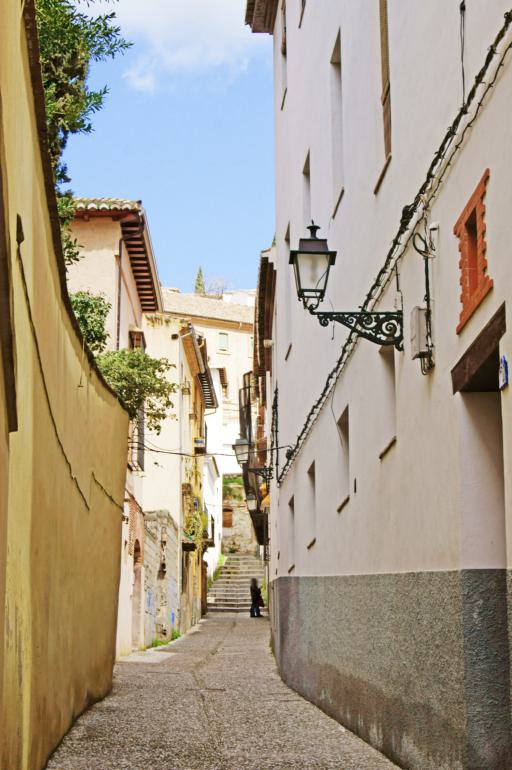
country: ES
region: Andalusia
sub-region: Provincia de Granada
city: Granada
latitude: 37.1788
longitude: -3.5904
